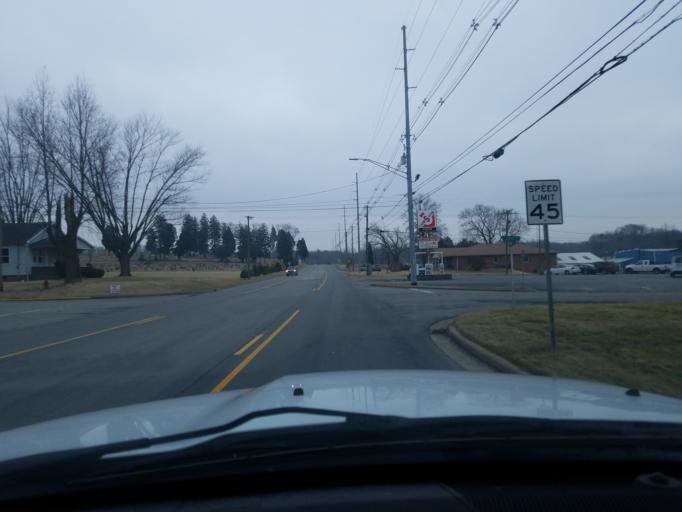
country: US
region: Indiana
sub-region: Perry County
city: Tell City
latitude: 37.9628
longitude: -86.7543
